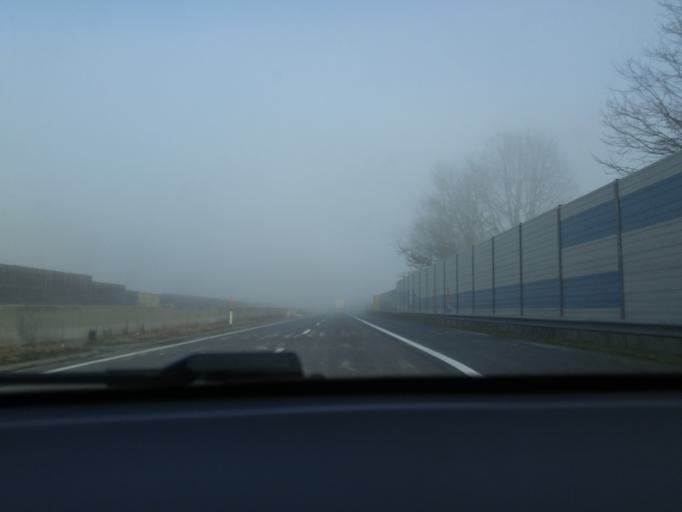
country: AT
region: Upper Austria
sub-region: Politischer Bezirk Vocklabruck
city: Sankt Georgen im Attergau
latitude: 47.9252
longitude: 13.5050
